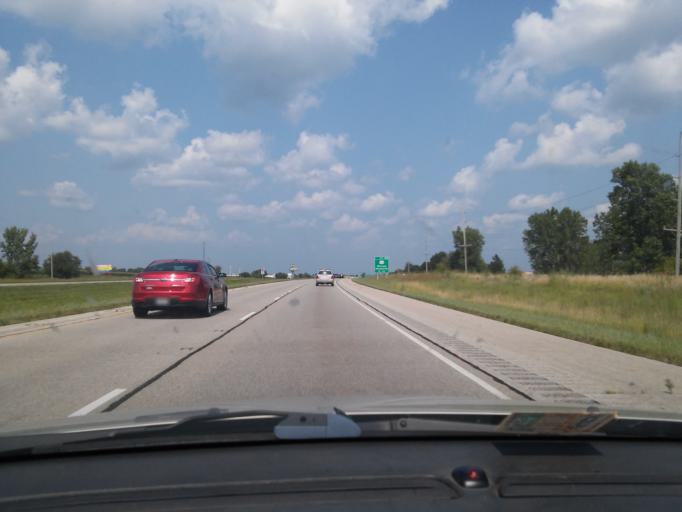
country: US
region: Illinois
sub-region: Logan County
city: Atlanta
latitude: 40.3040
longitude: -89.1792
